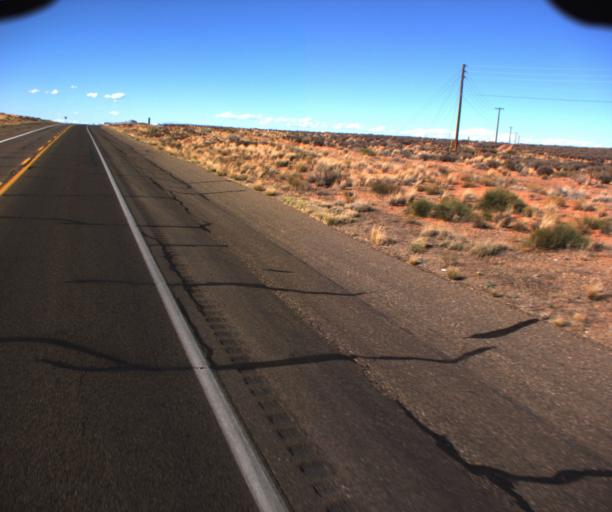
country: US
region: Arizona
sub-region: Coconino County
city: Page
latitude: 36.9584
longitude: -111.5050
